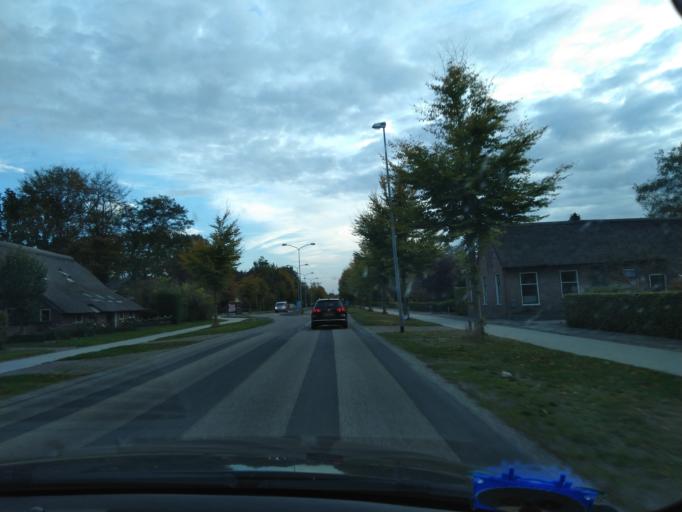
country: NL
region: Drenthe
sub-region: Gemeente Tynaarlo
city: Vries
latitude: 53.0691
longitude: 6.5775
